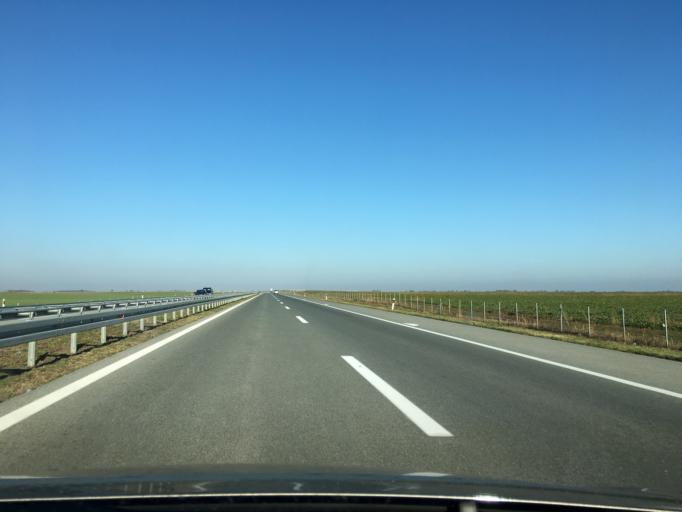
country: RS
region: Autonomna Pokrajina Vojvodina
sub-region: Severnobacki Okrug
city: Mali Igos
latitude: 45.7129
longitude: 19.7138
